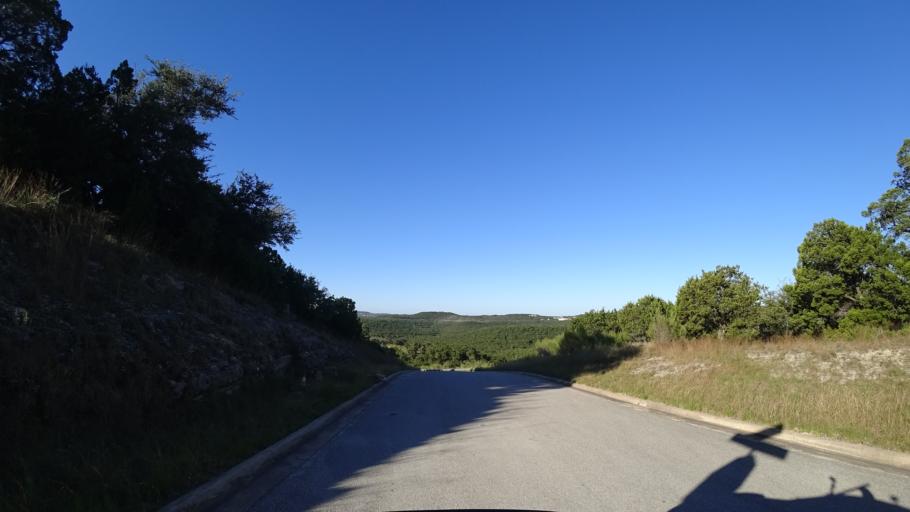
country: US
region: Texas
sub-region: Travis County
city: West Lake Hills
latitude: 30.3587
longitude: -97.8109
